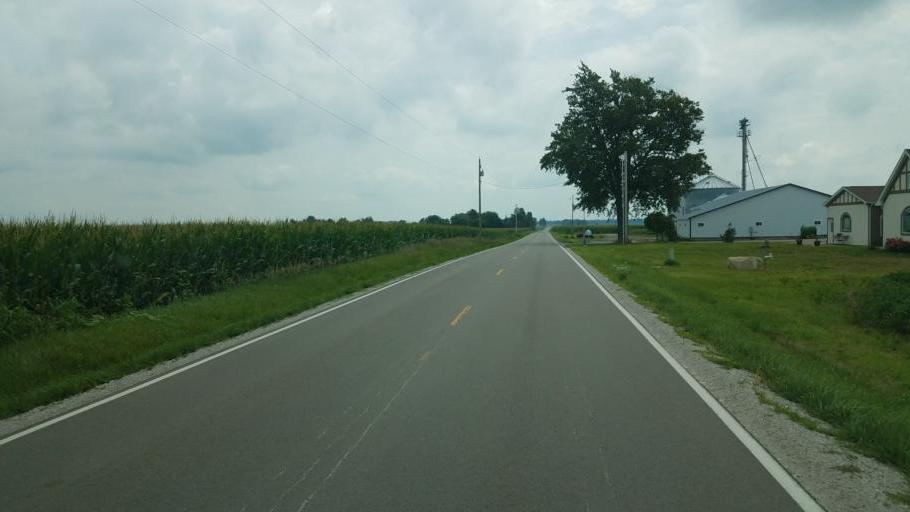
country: US
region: Ohio
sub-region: Crawford County
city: Bucyrus
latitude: 40.7180
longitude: -82.9838
